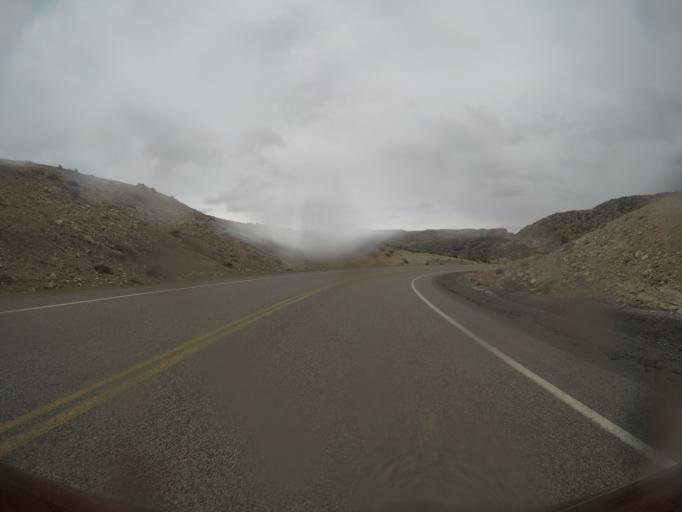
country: US
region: Wyoming
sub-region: Big Horn County
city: Lovell
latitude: 45.0481
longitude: -108.2532
